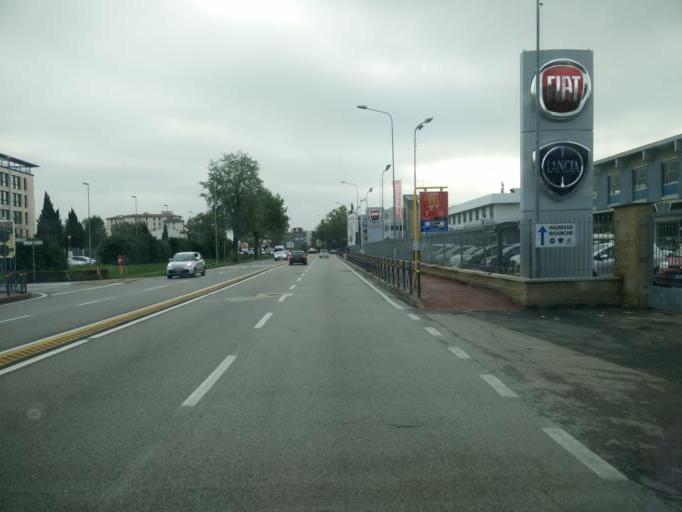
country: IT
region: Tuscany
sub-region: Province of Florence
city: Mantignano-Ugnano
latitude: 43.8051
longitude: 11.1812
